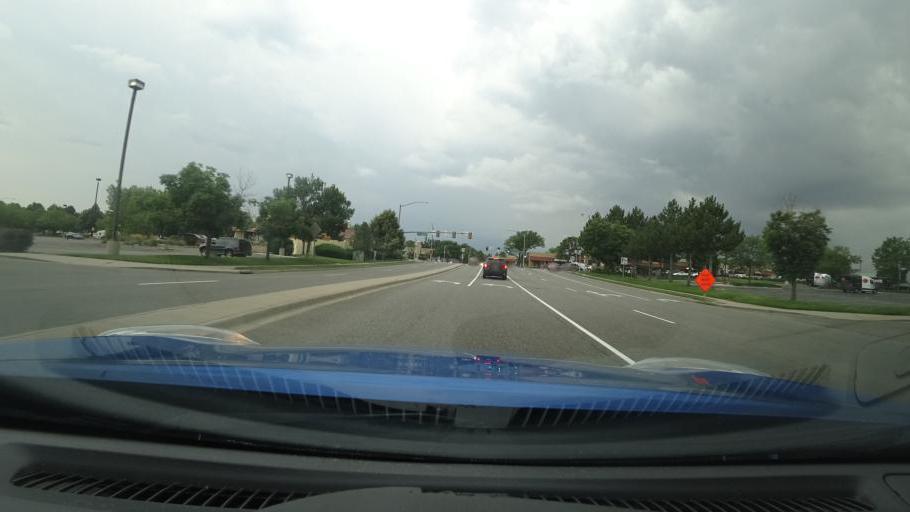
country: US
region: Colorado
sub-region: Adams County
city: Aurora
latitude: 39.6976
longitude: -104.8261
